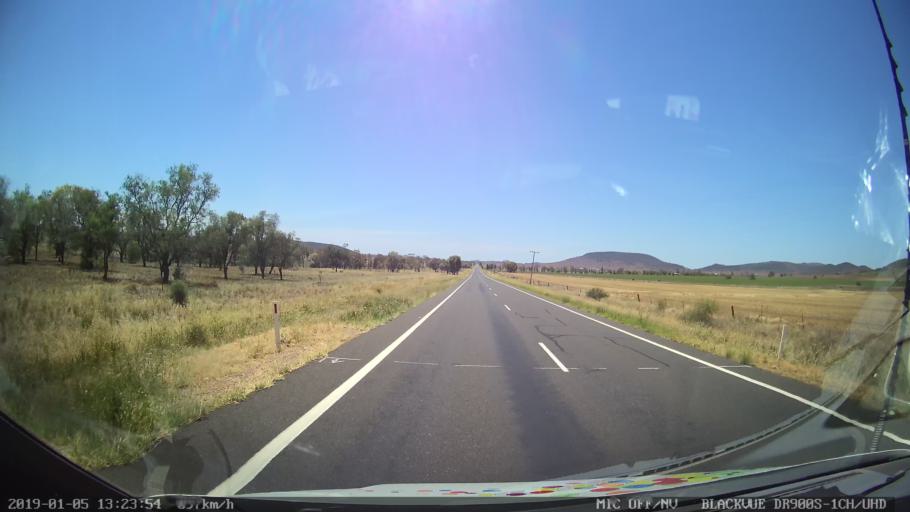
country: AU
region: New South Wales
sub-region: Gunnedah
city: Gunnedah
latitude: -31.0741
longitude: 149.9815
